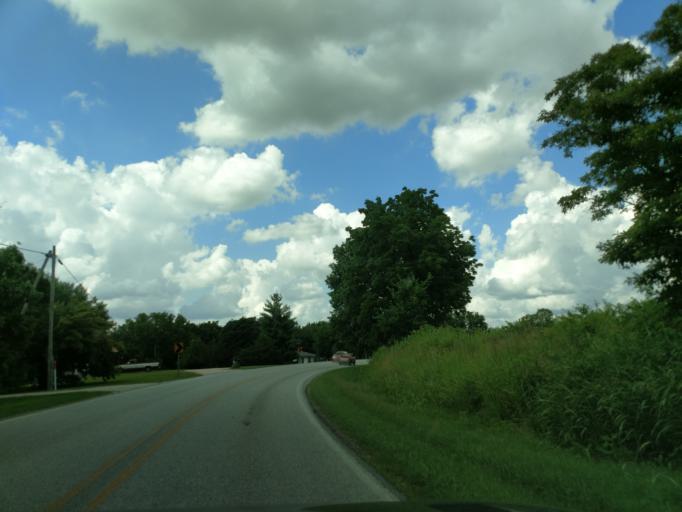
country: US
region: Arkansas
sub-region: Carroll County
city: Berryville
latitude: 36.4054
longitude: -93.5659
